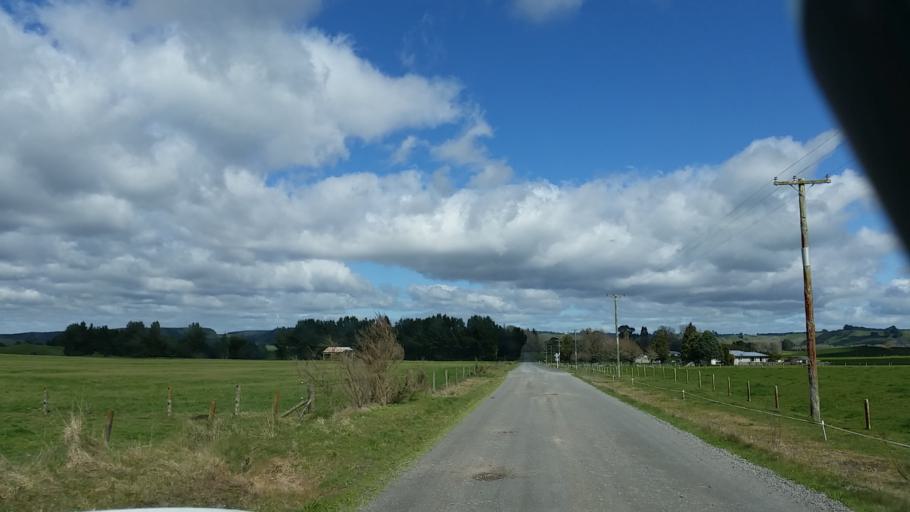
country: NZ
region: Bay of Plenty
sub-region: Whakatane District
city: Murupara
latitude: -38.3116
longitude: 176.5562
